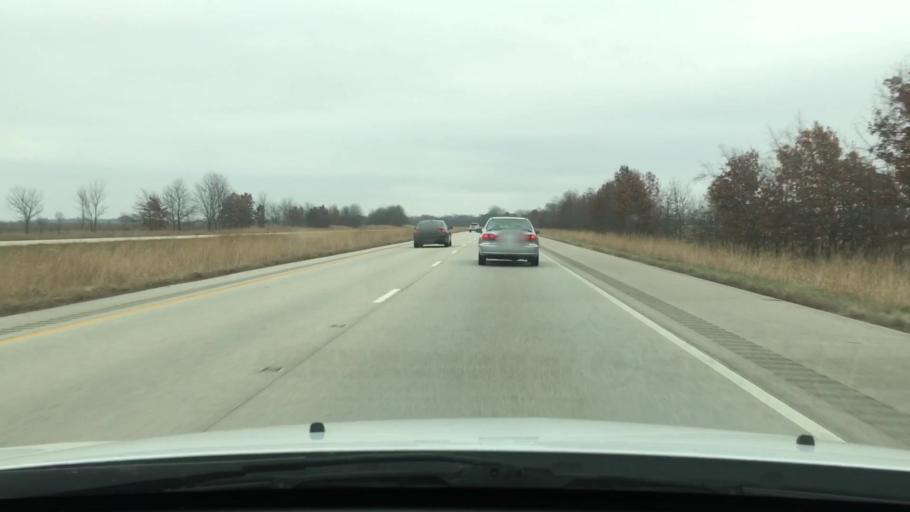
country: US
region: Illinois
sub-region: Sangamon County
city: New Berlin
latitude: 39.7411
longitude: -89.8353
